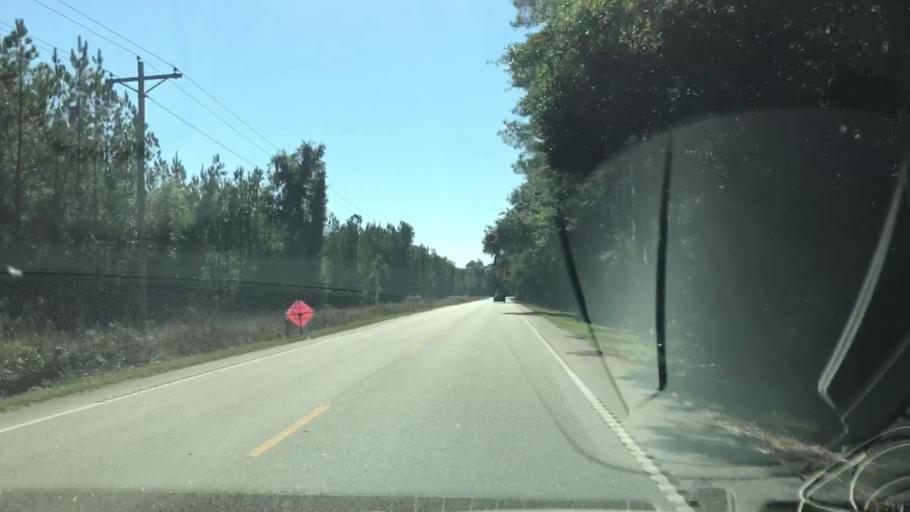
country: US
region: South Carolina
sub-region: Jasper County
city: Ridgeland
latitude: 32.5010
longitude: -80.8861
